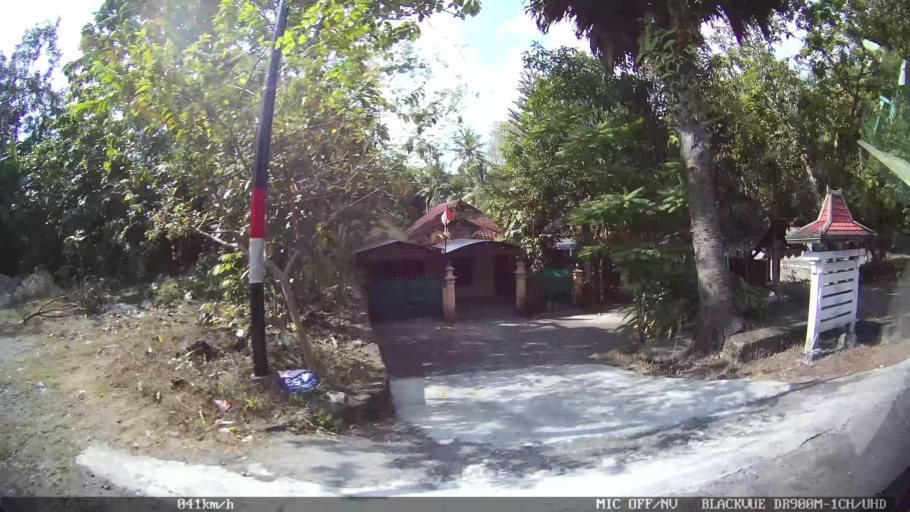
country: ID
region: Daerah Istimewa Yogyakarta
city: Kasihan
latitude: -7.8416
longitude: 110.3092
